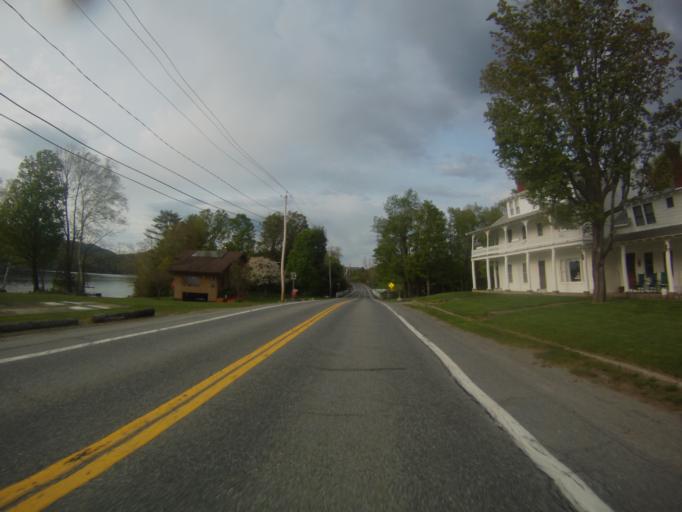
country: US
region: New York
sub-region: Warren County
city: Warrensburg
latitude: 43.7048
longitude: -73.7095
